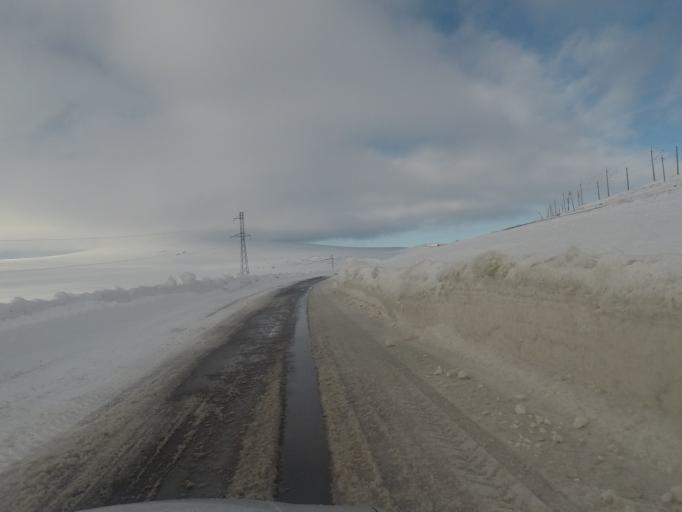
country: GE
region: Kvemo Kartli
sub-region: Tsalka
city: Tsalka
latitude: 41.4790
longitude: 43.8505
